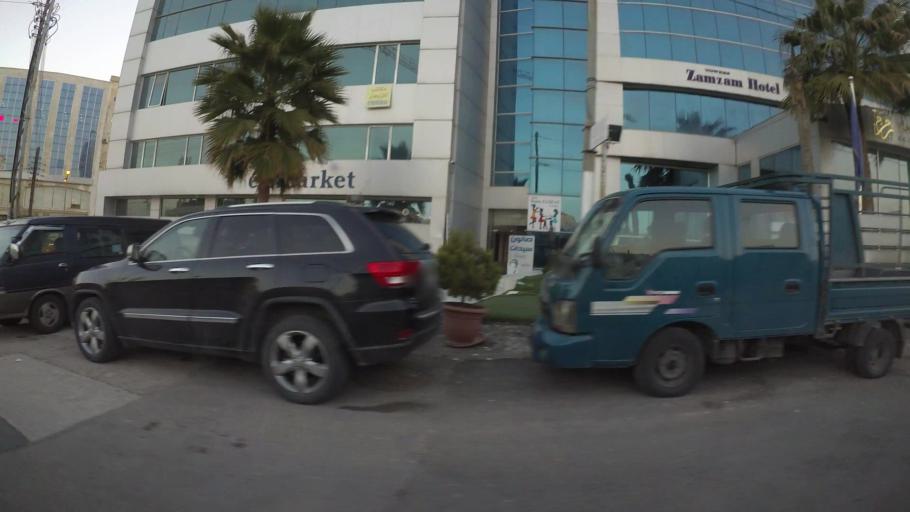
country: JO
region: Amman
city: Al Jubayhah
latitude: 31.9976
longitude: 35.8535
